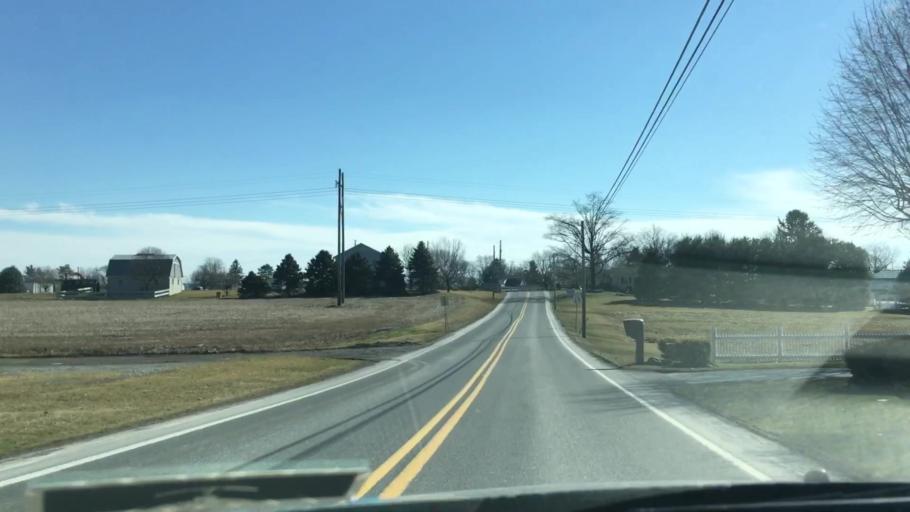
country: US
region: Pennsylvania
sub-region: Lancaster County
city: Reamstown
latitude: 40.1745
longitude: -76.1262
